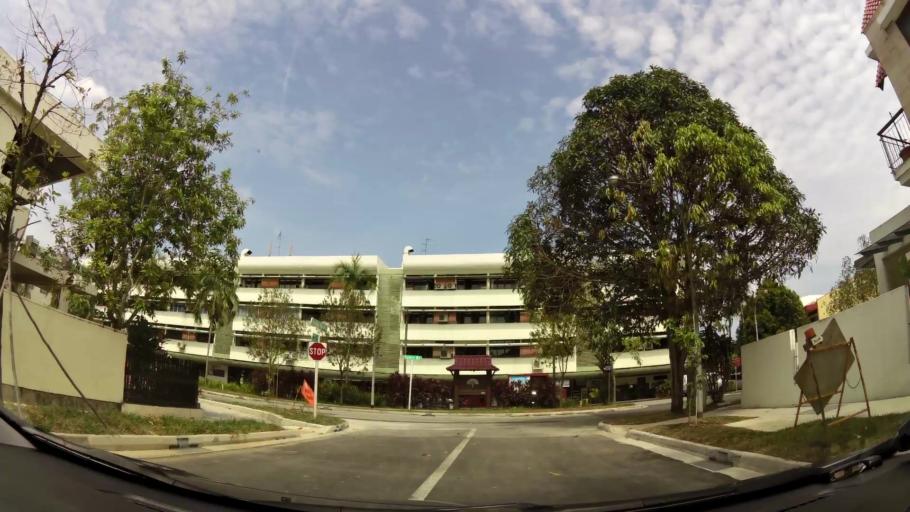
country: SG
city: Singapore
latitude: 1.3203
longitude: 103.7569
